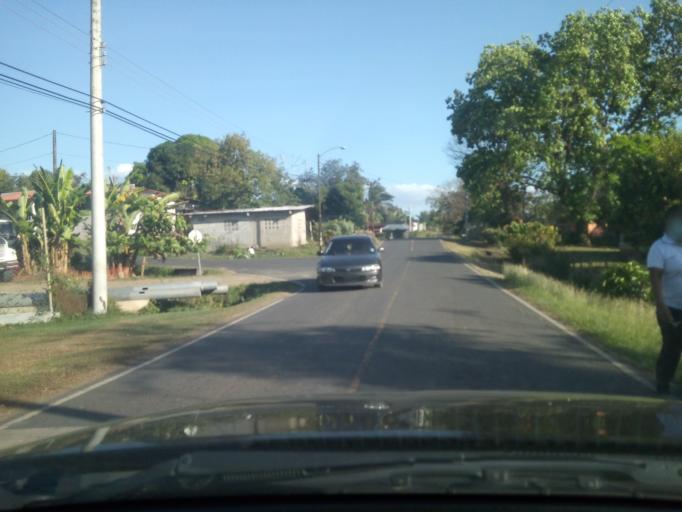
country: PA
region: Veraguas
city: Atalaya
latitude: 8.0439
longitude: -80.9277
